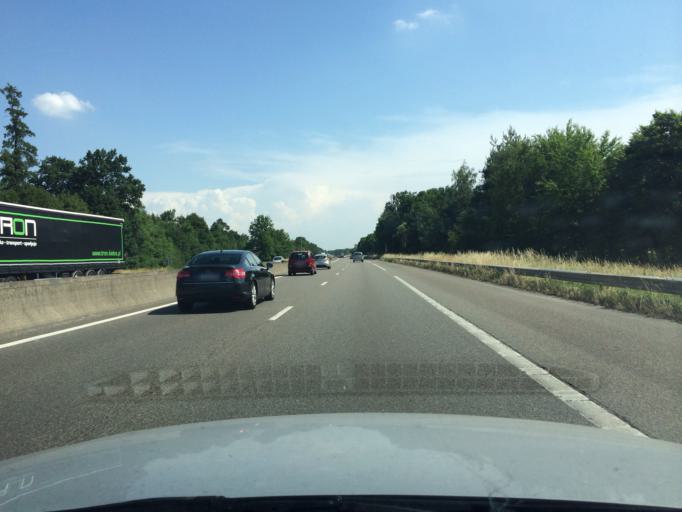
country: FR
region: Alsace
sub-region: Departement du Bas-Rhin
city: Brumath
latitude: 48.7258
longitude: 7.6914
